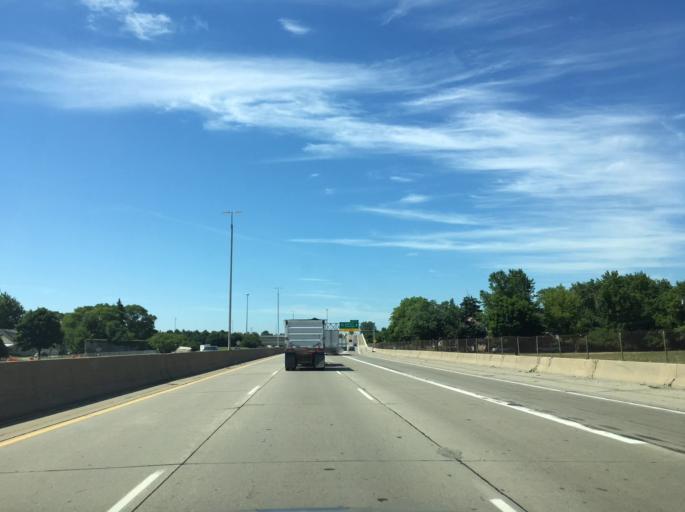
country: US
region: Michigan
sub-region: Wayne County
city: Allen Park
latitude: 42.2734
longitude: -83.2209
